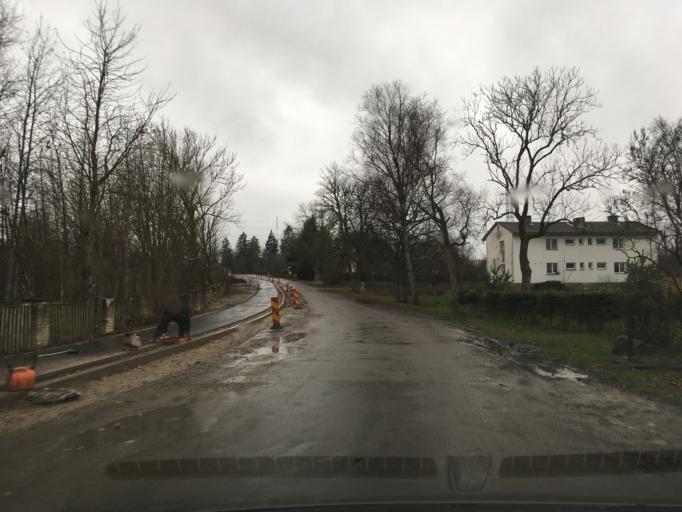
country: EE
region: Laeaene
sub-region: Lihula vald
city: Lihula
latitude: 58.6821
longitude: 23.8234
